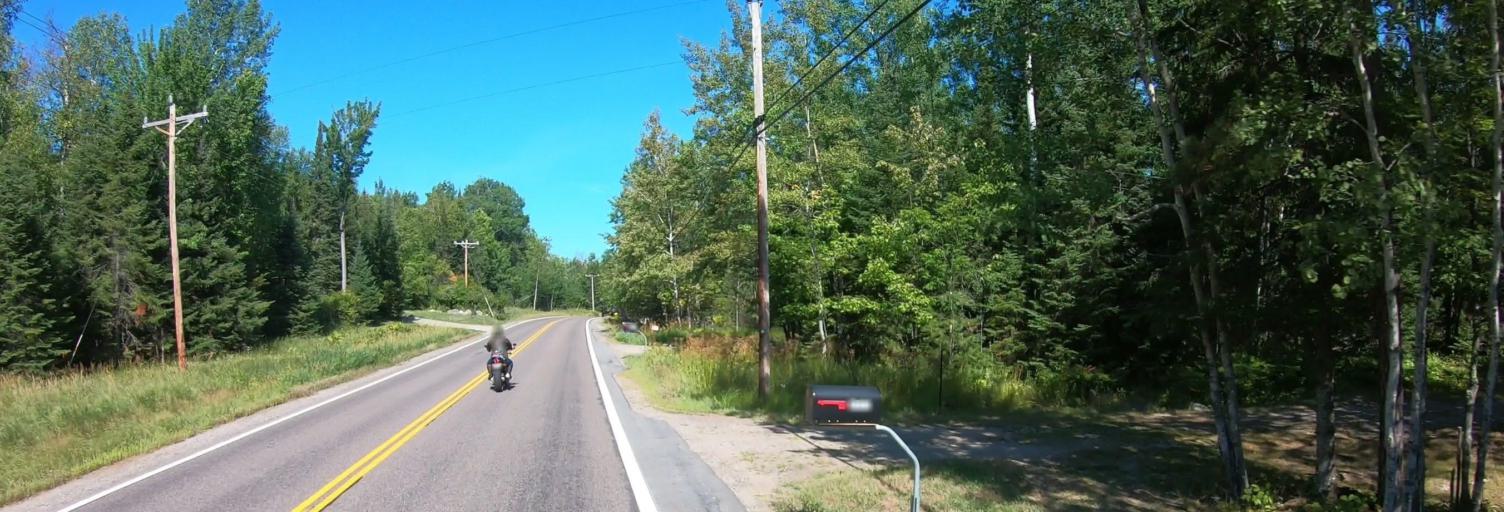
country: US
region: Minnesota
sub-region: Saint Louis County
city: Mountain Iron
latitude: 47.9304
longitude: -92.6719
